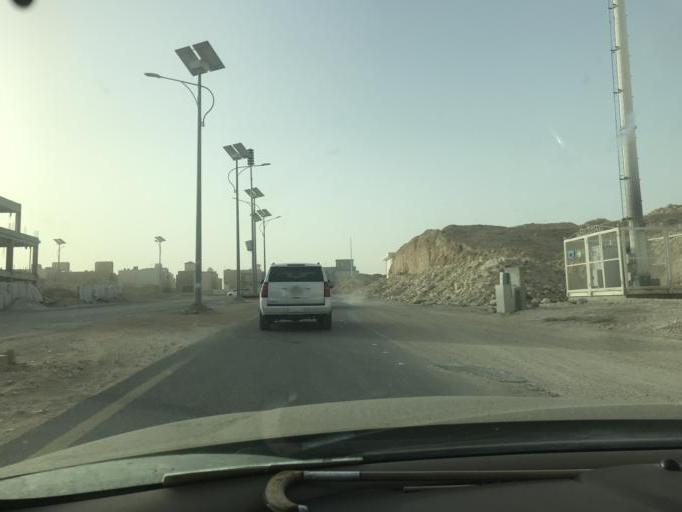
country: SA
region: Ar Riyad
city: Riyadh
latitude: 24.8393
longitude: 46.6674
